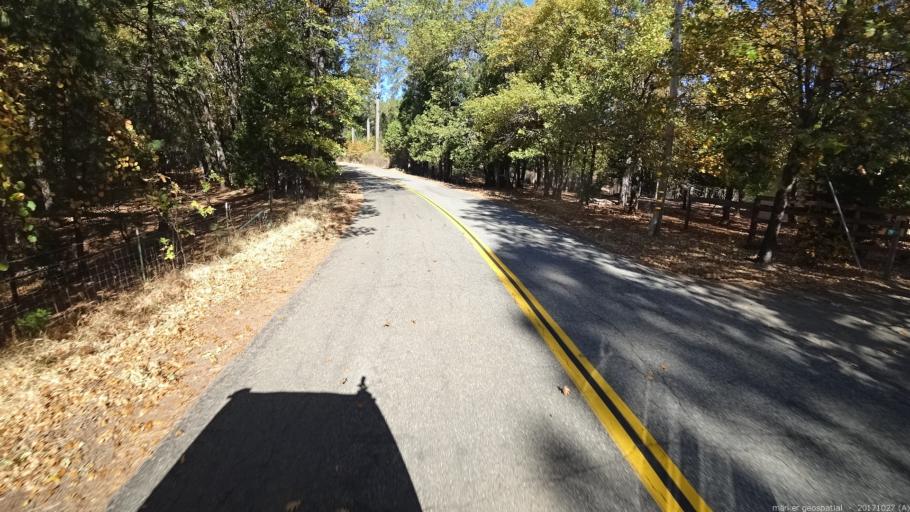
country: US
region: California
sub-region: Shasta County
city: Burney
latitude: 40.8257
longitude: -121.9398
